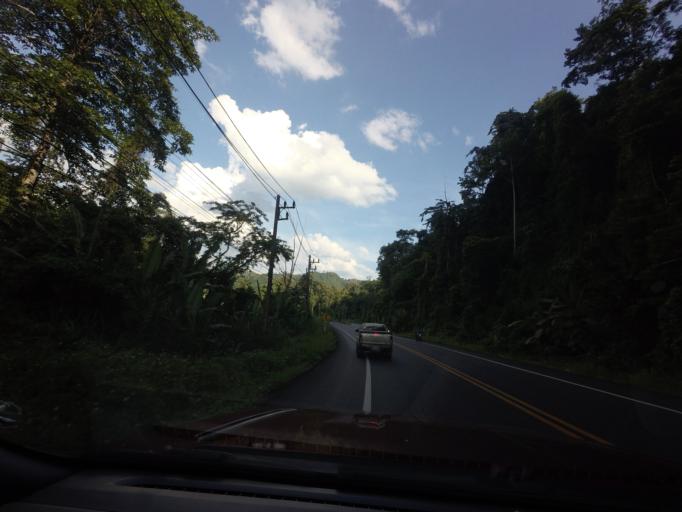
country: TH
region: Yala
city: Than To
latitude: 6.2039
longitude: 101.1702
